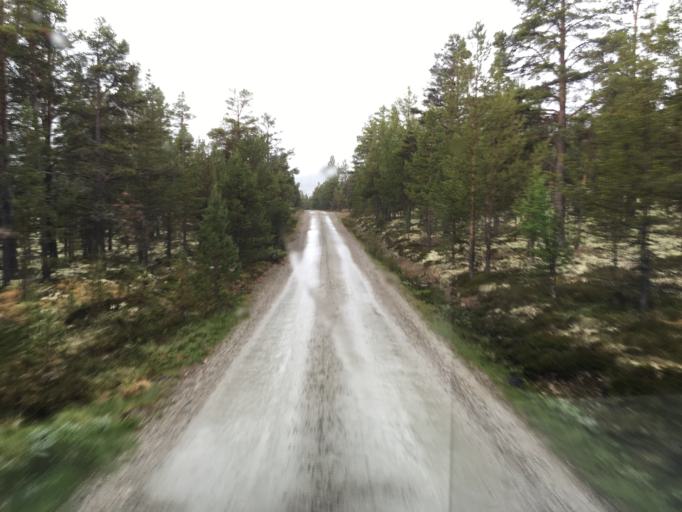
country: NO
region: Hedmark
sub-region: Folldal
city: Folldal
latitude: 62.0692
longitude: 9.9383
